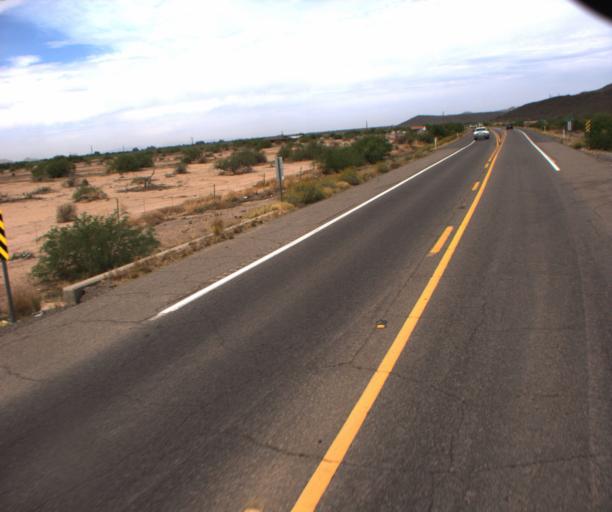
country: US
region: Arizona
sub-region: Pinal County
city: Sacaton
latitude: 33.1002
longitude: -111.7118
